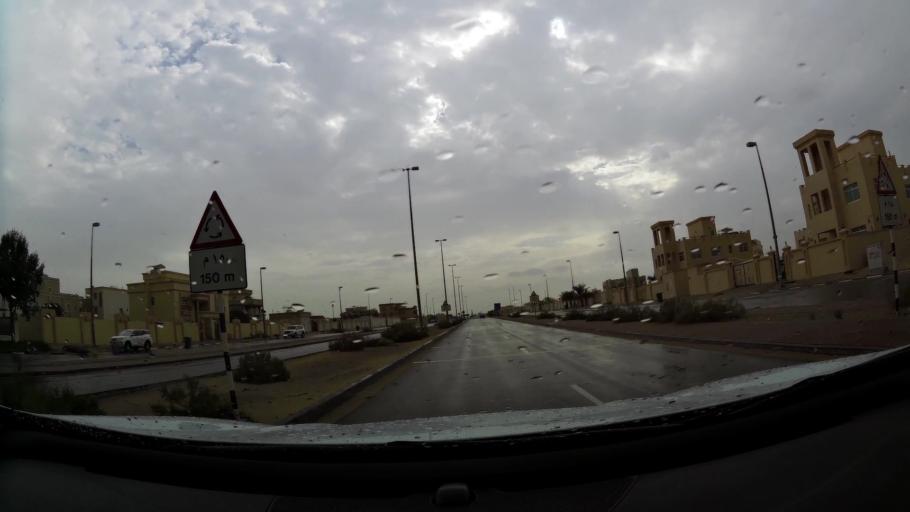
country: AE
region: Abu Dhabi
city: Abu Dhabi
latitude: 24.3582
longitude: 54.6292
